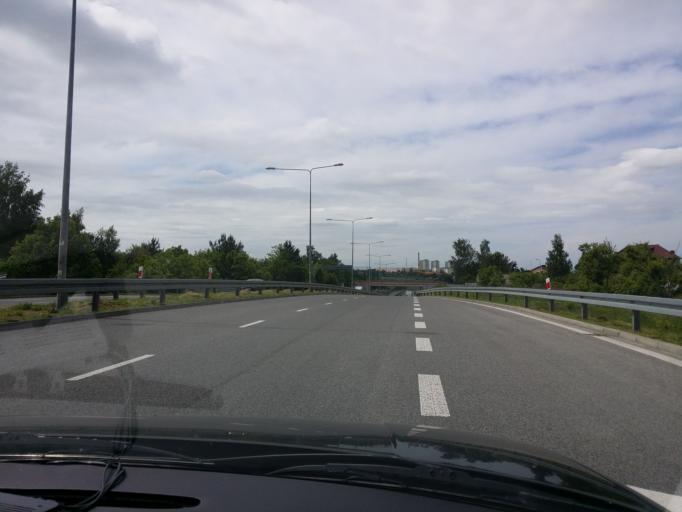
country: PL
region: Masovian Voivodeship
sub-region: Powiat radomski
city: Trablice
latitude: 51.3702
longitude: 21.1525
